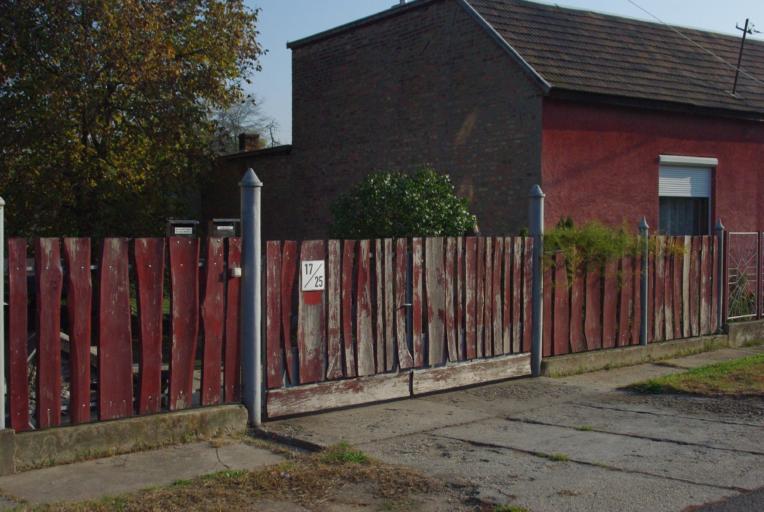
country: HU
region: Komarom-Esztergom
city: Dorog
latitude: 47.7190
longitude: 18.7461
